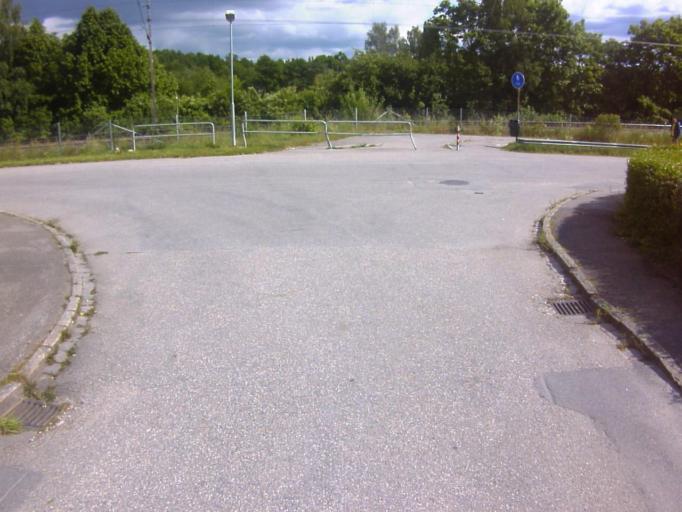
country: SE
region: Soedermanland
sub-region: Eskilstuna Kommun
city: Eskilstuna
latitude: 59.3539
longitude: 16.5031
